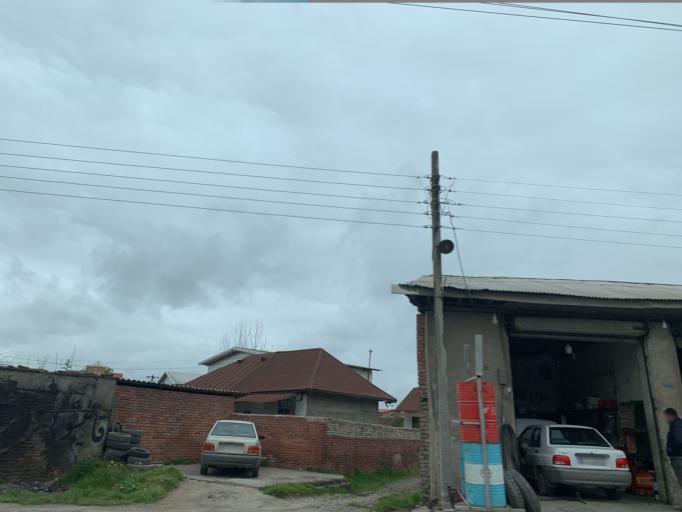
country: IR
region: Mazandaran
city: Babol
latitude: 36.5094
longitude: 52.5484
